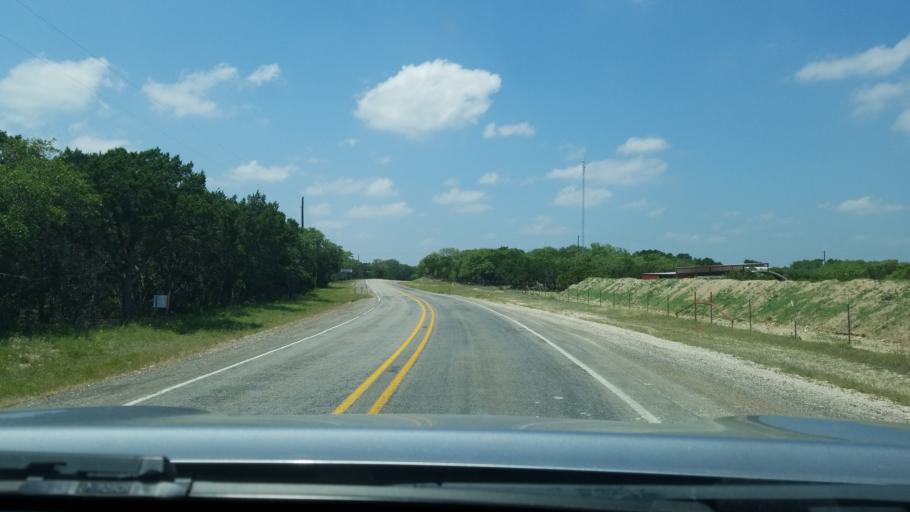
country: US
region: Texas
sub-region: Hays County
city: Woodcreek
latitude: 30.0492
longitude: -98.2002
